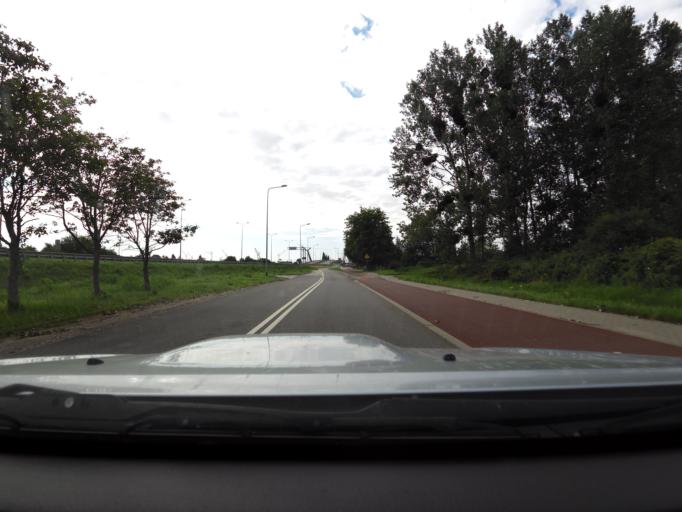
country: PL
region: Pomeranian Voivodeship
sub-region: Gdansk
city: Gdansk
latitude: 54.3639
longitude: 18.6890
